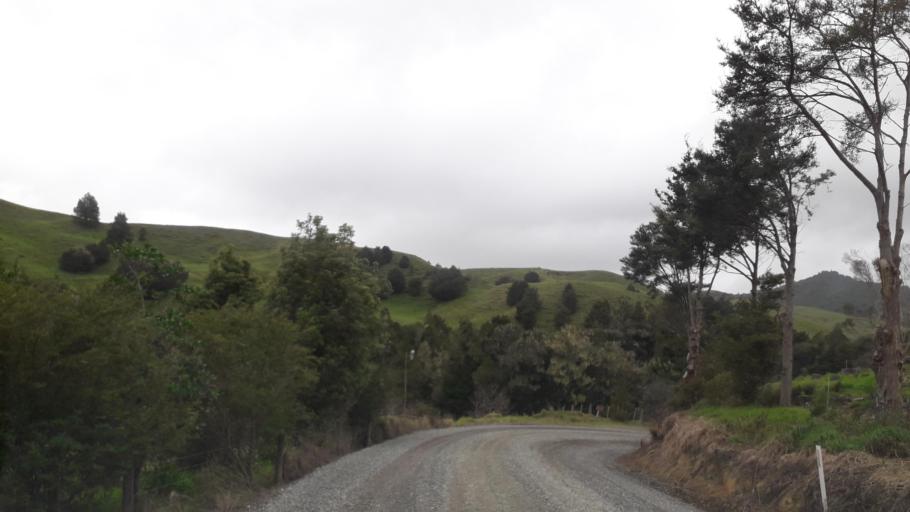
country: NZ
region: Northland
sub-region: Far North District
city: Waimate North
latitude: -35.1311
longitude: 173.7181
